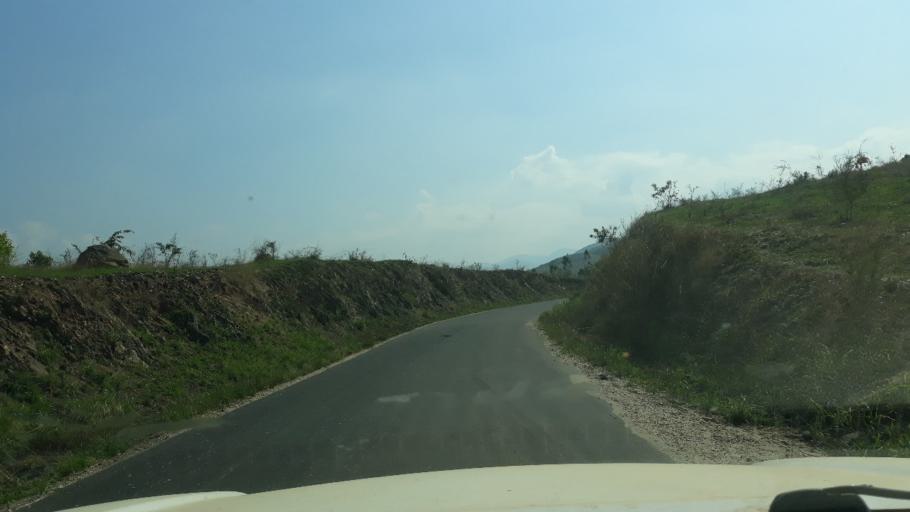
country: CD
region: South Kivu
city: Uvira
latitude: -3.2012
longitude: 29.1572
